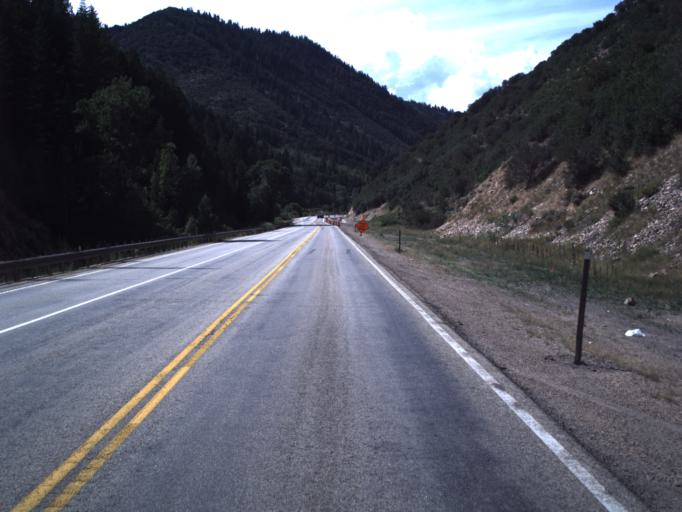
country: US
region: Utah
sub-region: Wasatch County
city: Heber
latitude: 40.3546
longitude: -111.2782
